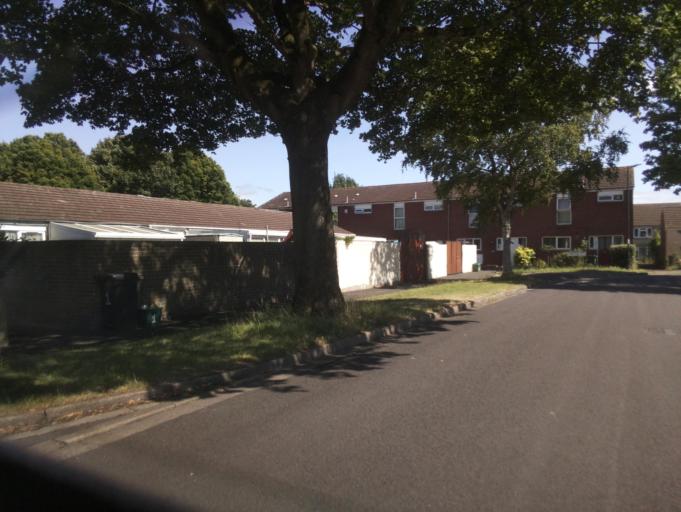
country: GB
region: England
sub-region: Bristol
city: Bristol
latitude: 51.5080
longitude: -2.6048
